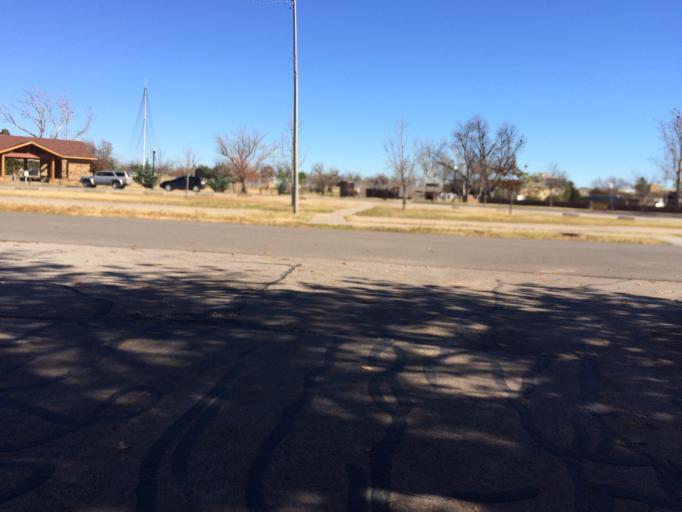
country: US
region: Oklahoma
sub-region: Cleveland County
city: Norman
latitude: 35.2236
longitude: -97.4495
